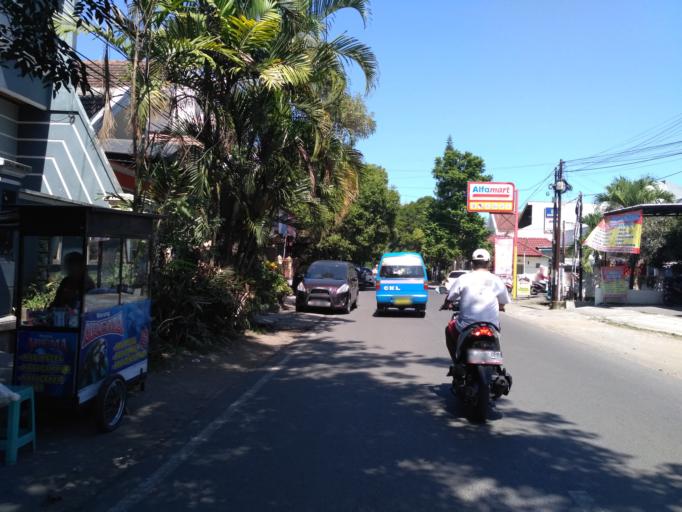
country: ID
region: East Java
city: Malang
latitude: -7.9740
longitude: 112.6662
